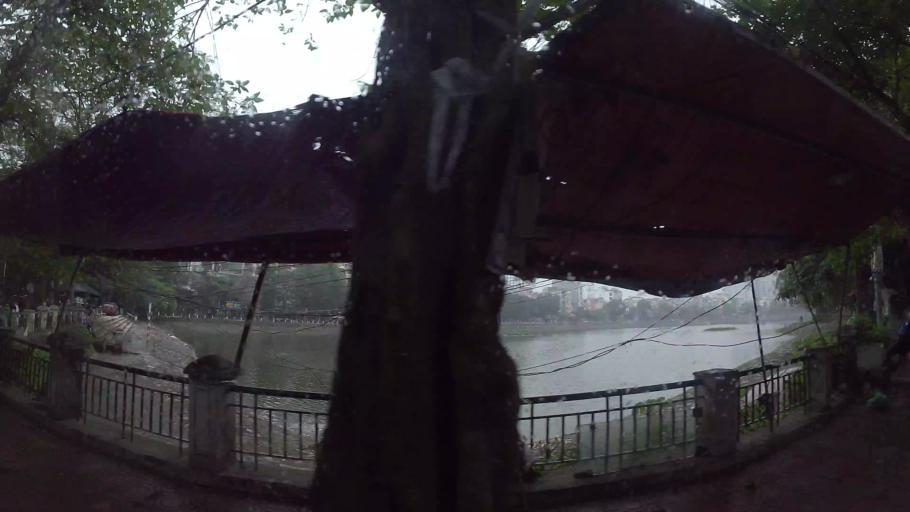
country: VN
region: Ha Noi
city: Dong Da
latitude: 21.0167
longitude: 105.8178
